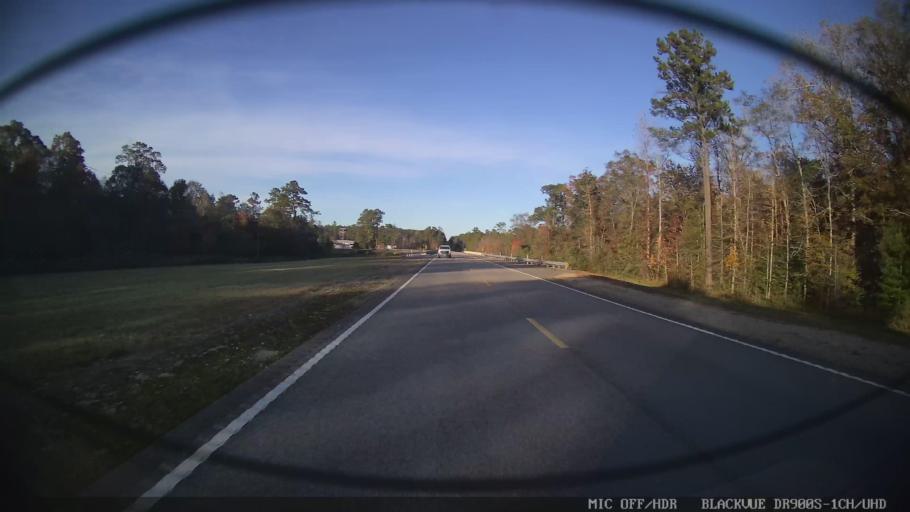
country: US
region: Mississippi
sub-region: Lamar County
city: Purvis
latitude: 31.0707
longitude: -89.4216
